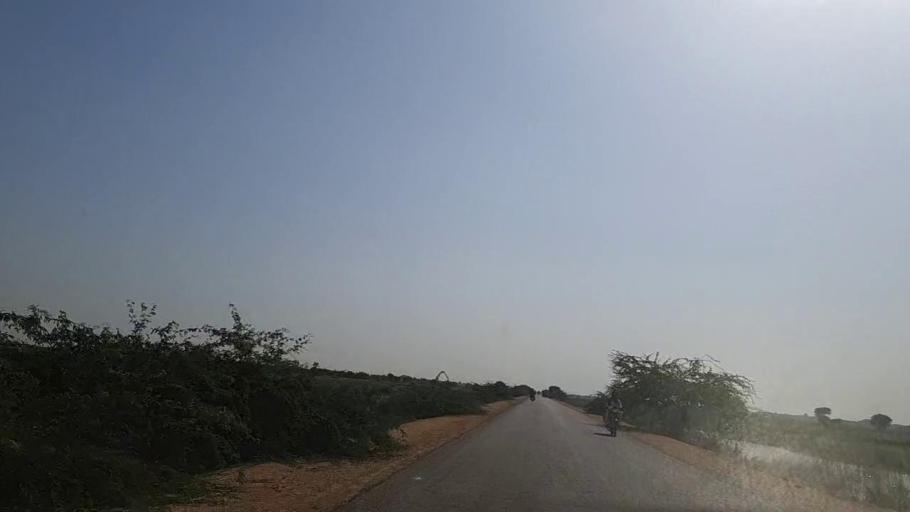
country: PK
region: Sindh
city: Mirpur Batoro
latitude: 24.5889
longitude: 68.2914
